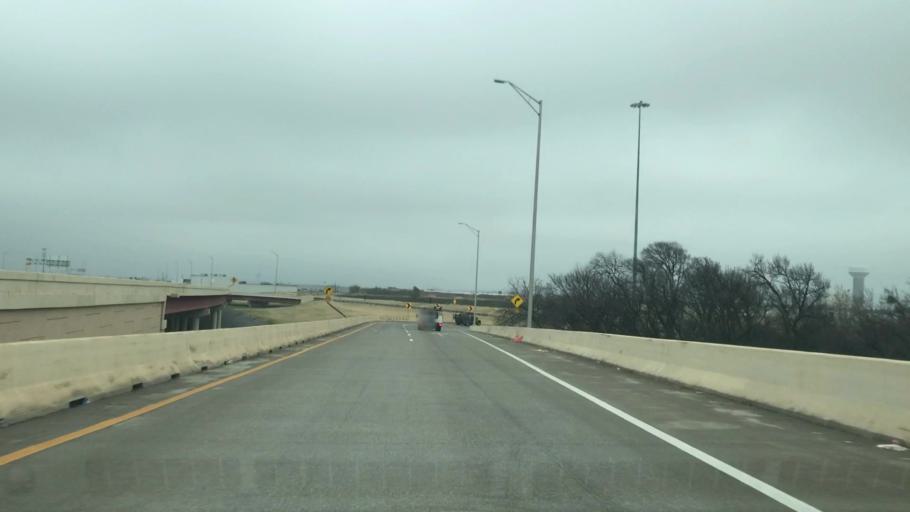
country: US
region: Texas
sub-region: Dallas County
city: Farmers Branch
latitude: 32.9174
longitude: -96.9339
